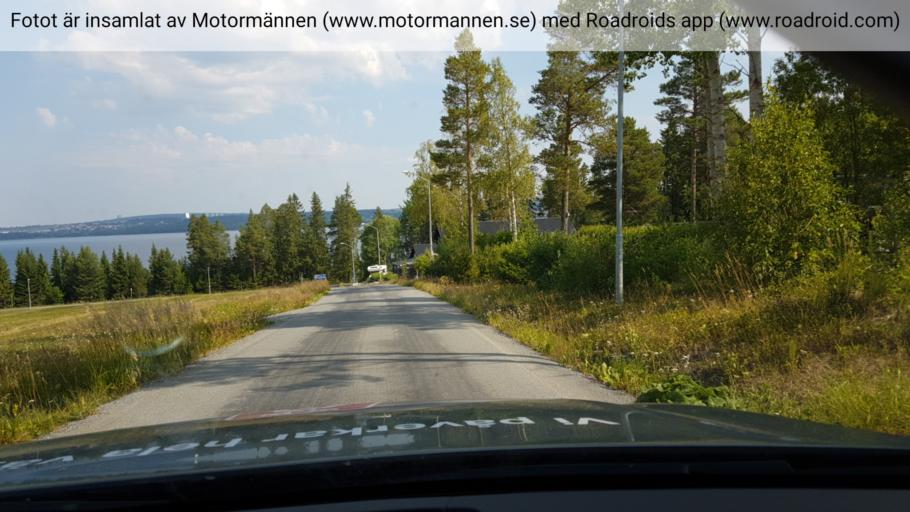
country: SE
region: Jaemtland
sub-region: OEstersunds Kommun
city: Ostersund
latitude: 63.1307
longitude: 14.6594
